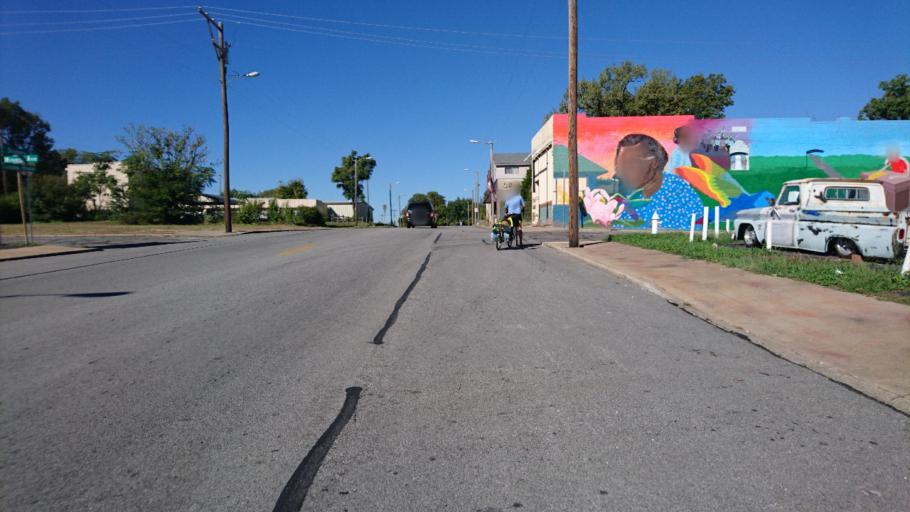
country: US
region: Missouri
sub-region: Jasper County
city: Joplin
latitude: 37.0920
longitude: -94.5057
